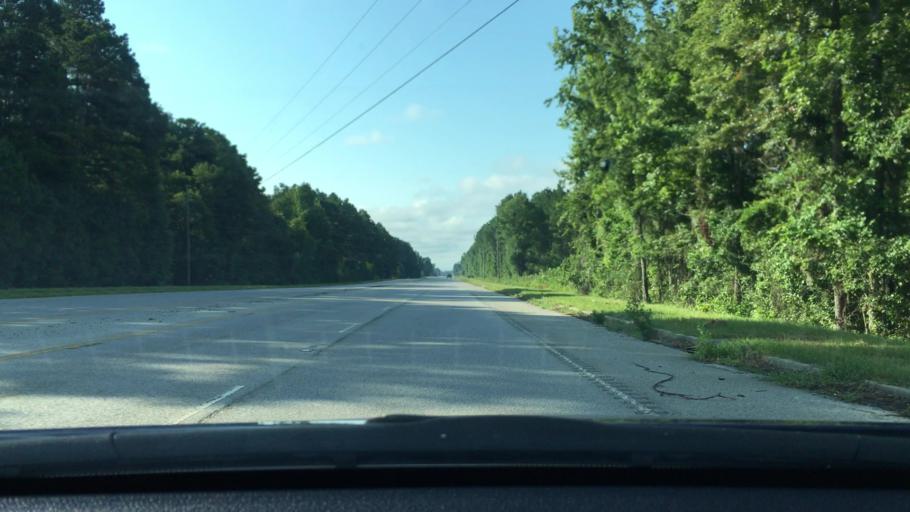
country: US
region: South Carolina
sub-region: Clarendon County
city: Manning
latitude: 33.7745
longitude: -80.2395
